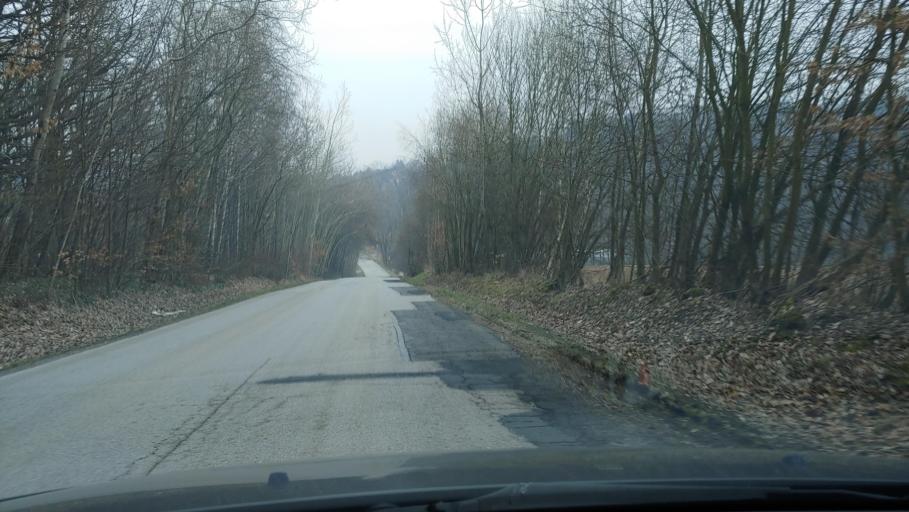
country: PL
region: Lesser Poland Voivodeship
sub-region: Powiat krakowski
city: Balice
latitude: 50.0955
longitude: 19.7586
